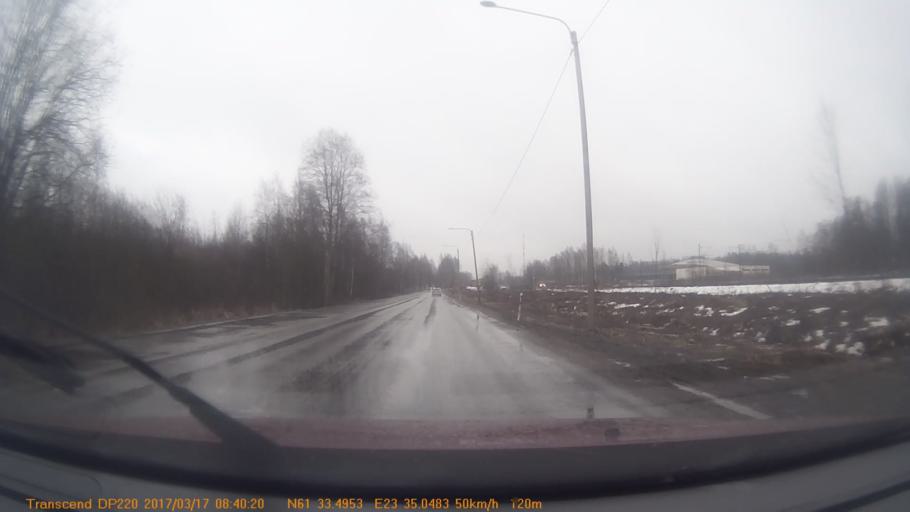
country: FI
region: Pirkanmaa
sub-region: Tampere
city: Yloejaervi
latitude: 61.5584
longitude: 23.5841
